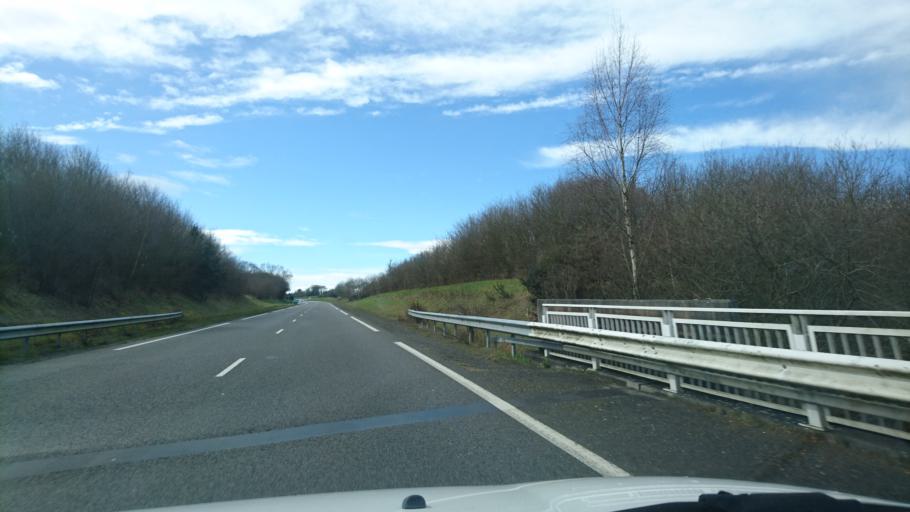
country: FR
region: Brittany
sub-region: Departement d'Ille-et-Vilaine
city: Chasne-sur-Illet
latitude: 48.2562
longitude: -1.6044
